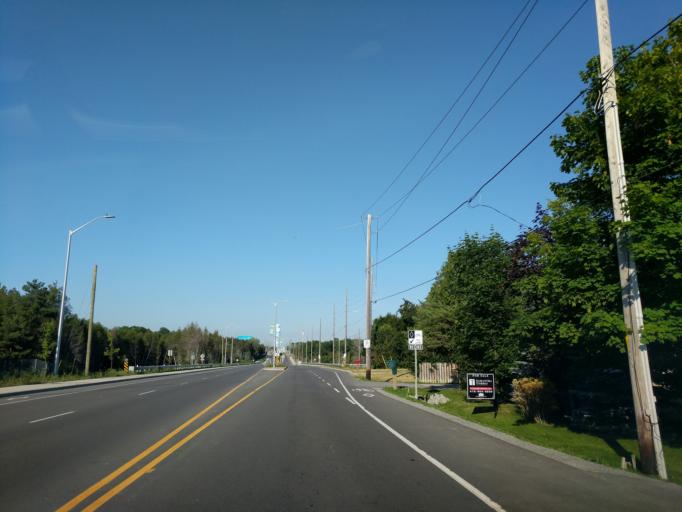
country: CA
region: Ontario
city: Oshawa
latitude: 43.9454
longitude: -78.9078
